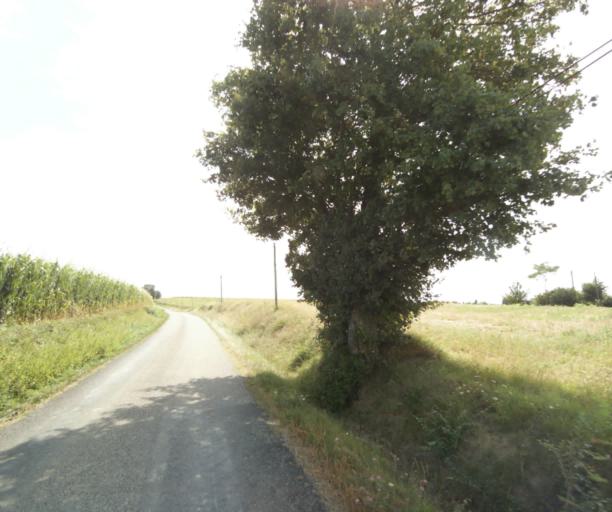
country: FR
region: Midi-Pyrenees
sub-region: Departement de la Haute-Garonne
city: Gaillac-Toulza
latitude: 43.2544
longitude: 1.4210
